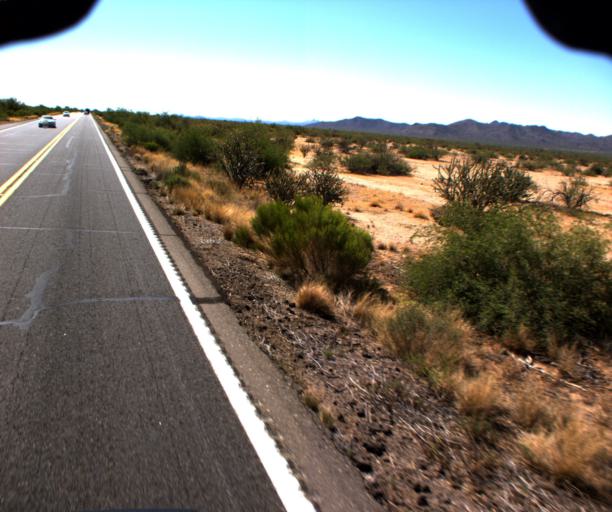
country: US
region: Arizona
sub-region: Yavapai County
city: Congress
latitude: 34.1395
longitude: -112.9738
